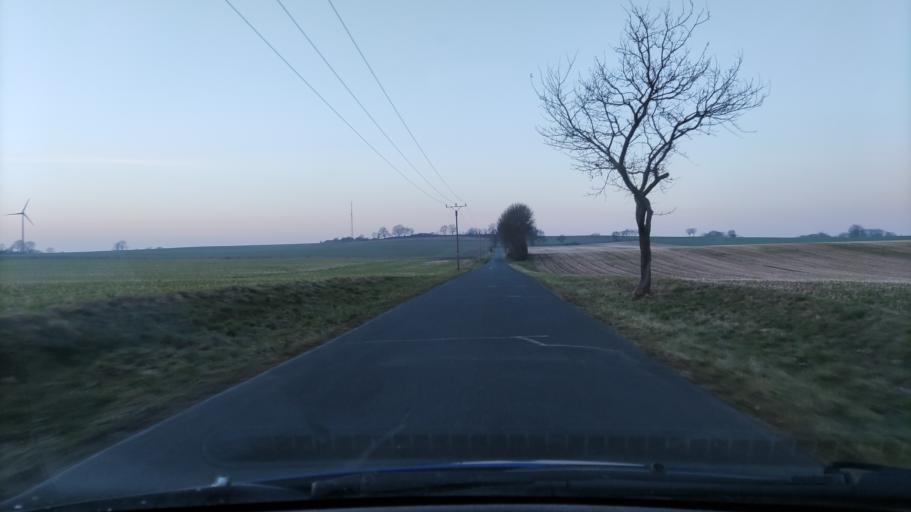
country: DE
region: Lower Saxony
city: Barum
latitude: 53.0430
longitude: 10.4802
